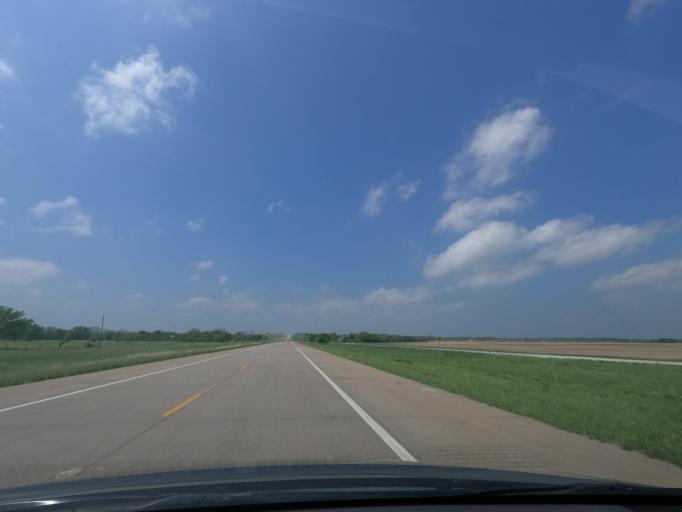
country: US
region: Kansas
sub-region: Wilson County
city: Fredonia
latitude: 37.5786
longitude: -95.8685
